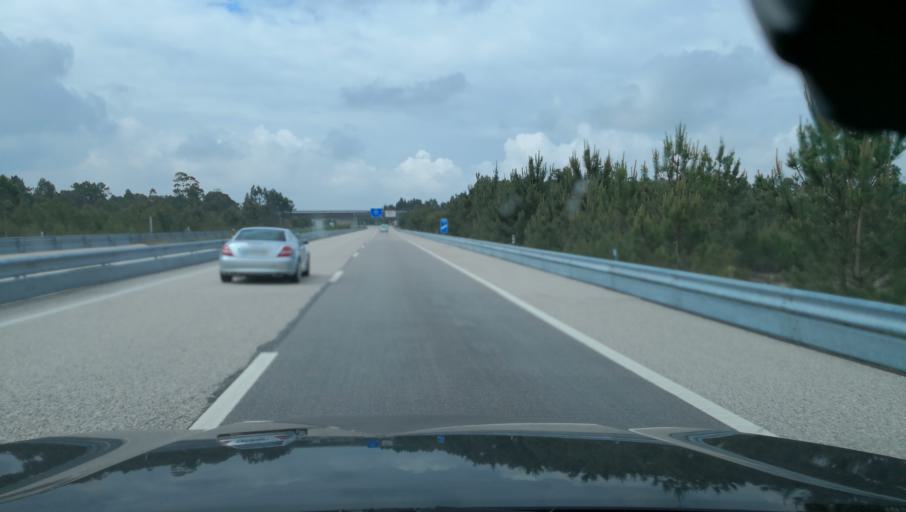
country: PT
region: Coimbra
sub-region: Montemor-O-Velho
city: Arazede
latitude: 40.3343
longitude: -8.7206
